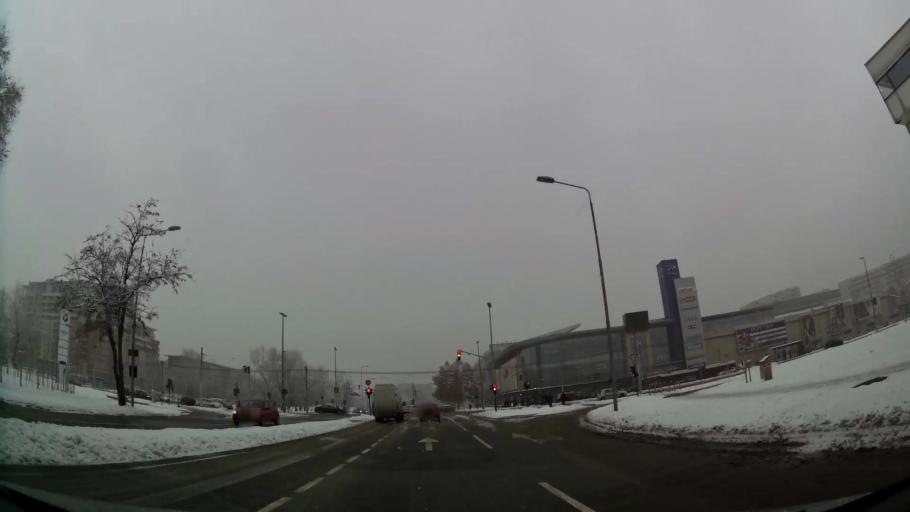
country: RS
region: Central Serbia
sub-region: Belgrade
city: Novi Beograd
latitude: 44.8038
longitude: 20.4040
